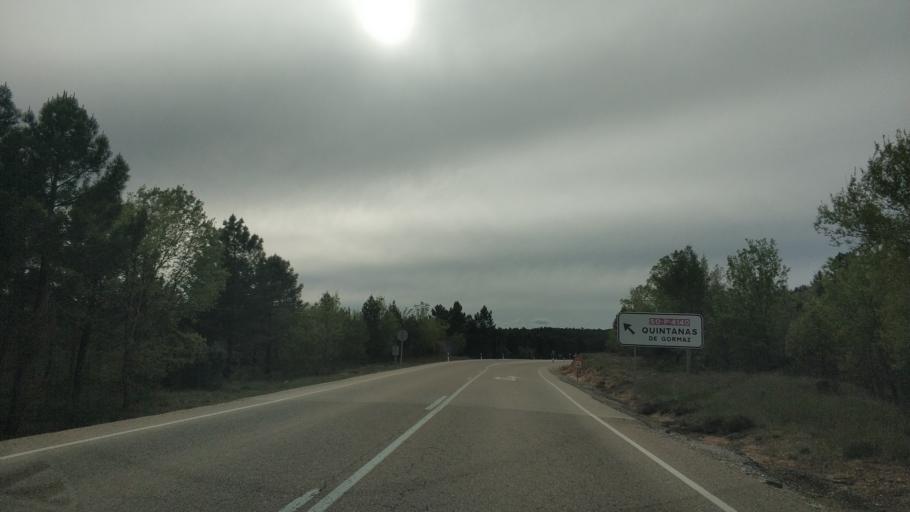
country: ES
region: Castille and Leon
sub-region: Provincia de Soria
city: Bayubas de Abajo
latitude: 41.5106
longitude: -2.9200
